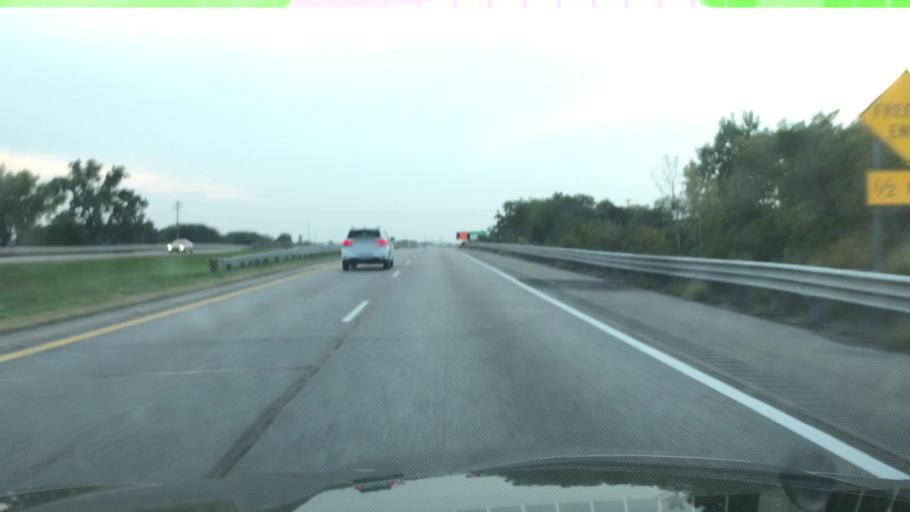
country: US
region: Michigan
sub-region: Macomb County
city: Sterling Heights
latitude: 42.6034
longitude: -83.0219
